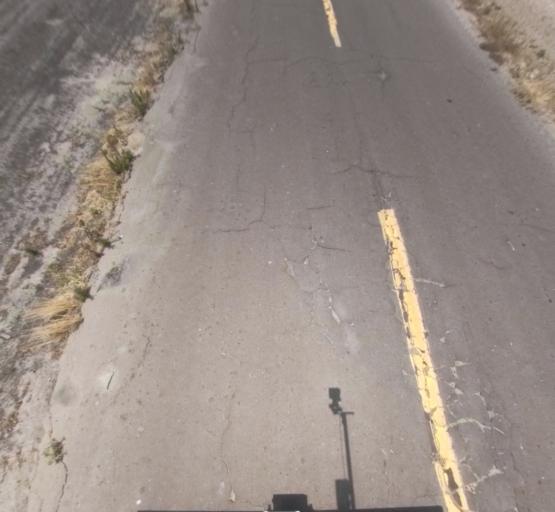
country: US
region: California
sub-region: Fresno County
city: Biola
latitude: 36.8222
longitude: -120.1071
